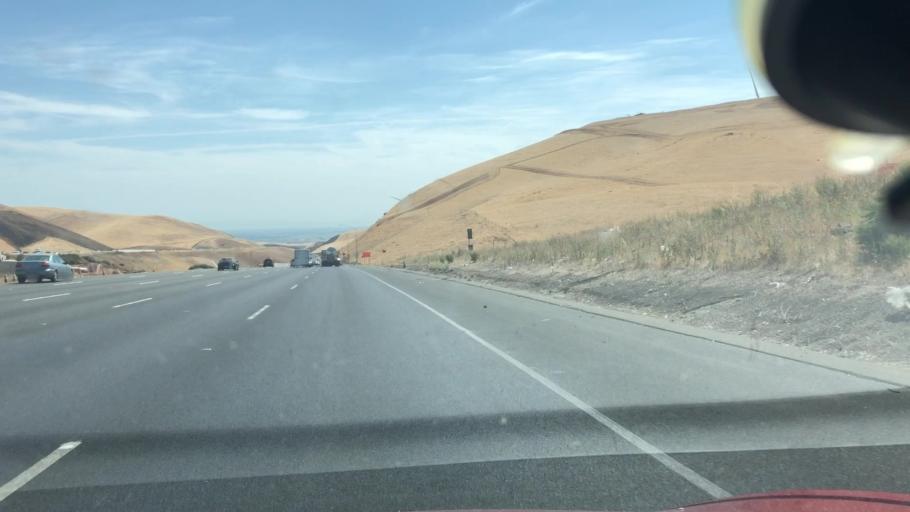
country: US
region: California
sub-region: Alameda County
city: Livermore
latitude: 37.7198
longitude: -121.6578
